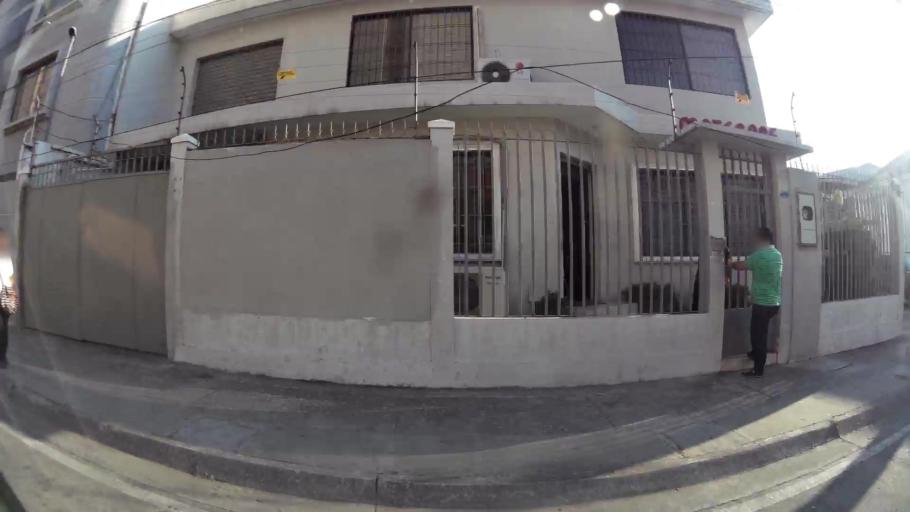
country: EC
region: Guayas
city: Eloy Alfaro
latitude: -2.1677
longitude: -79.8933
